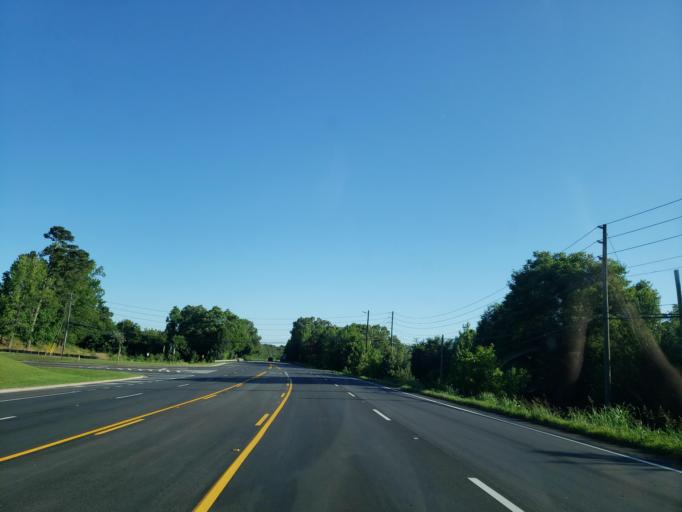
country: US
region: Georgia
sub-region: Floyd County
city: Rome
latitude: 34.3004
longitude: -85.1768
